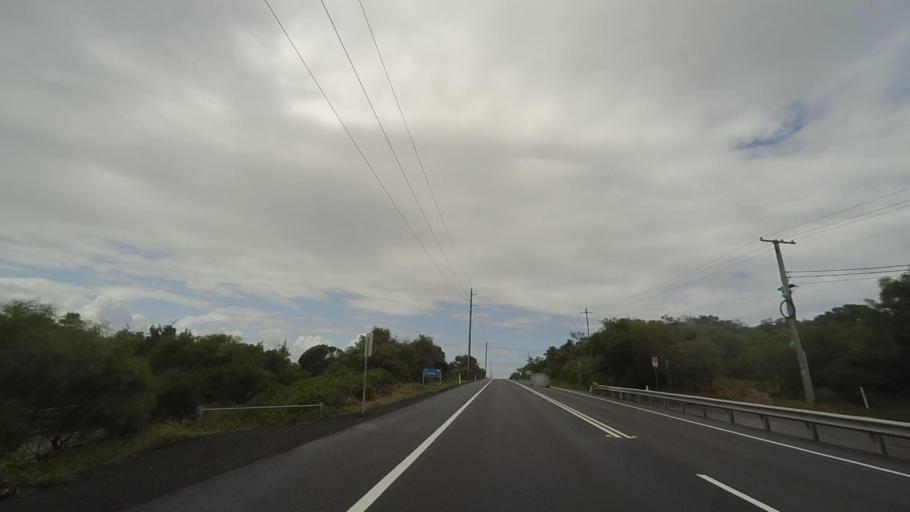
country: AU
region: New South Wales
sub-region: Wyong Shire
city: The Entrance
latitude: -33.3241
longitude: 151.5129
